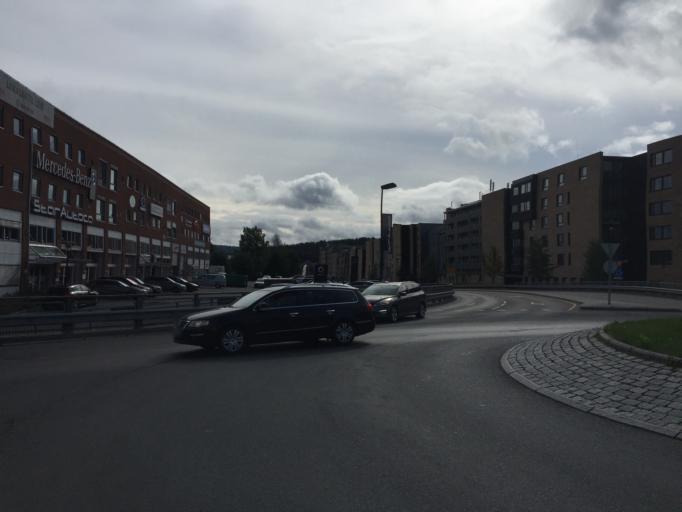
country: NO
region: Akershus
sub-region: Lorenskog
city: Kjenn
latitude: 59.9296
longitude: 10.9465
